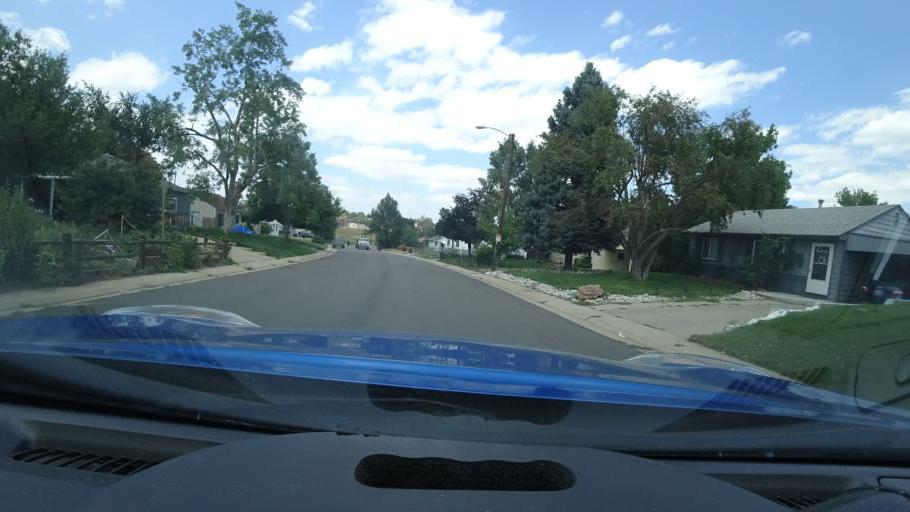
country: US
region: Colorado
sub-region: Arapahoe County
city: Sheridan
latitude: 39.6868
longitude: -105.0111
